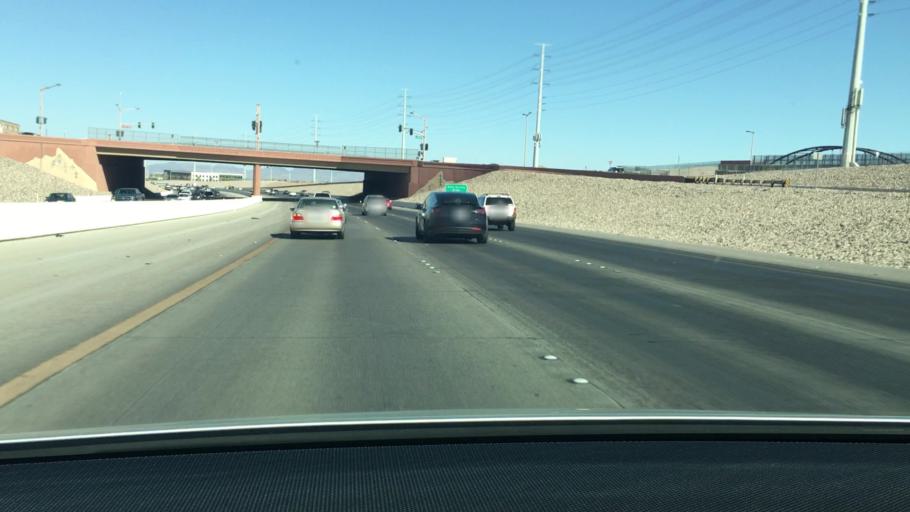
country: US
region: Nevada
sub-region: Clark County
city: Summerlin South
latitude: 36.1225
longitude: -115.3283
